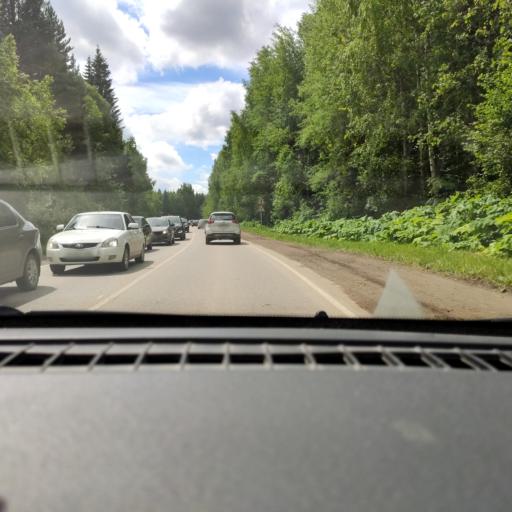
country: RU
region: Perm
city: Overyata
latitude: 58.1116
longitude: 55.8298
